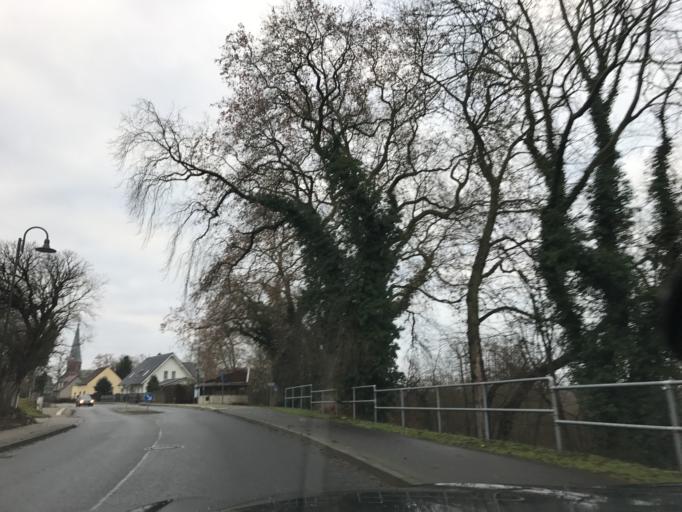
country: DE
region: Brandenburg
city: Werder
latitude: 52.3677
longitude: 12.9552
